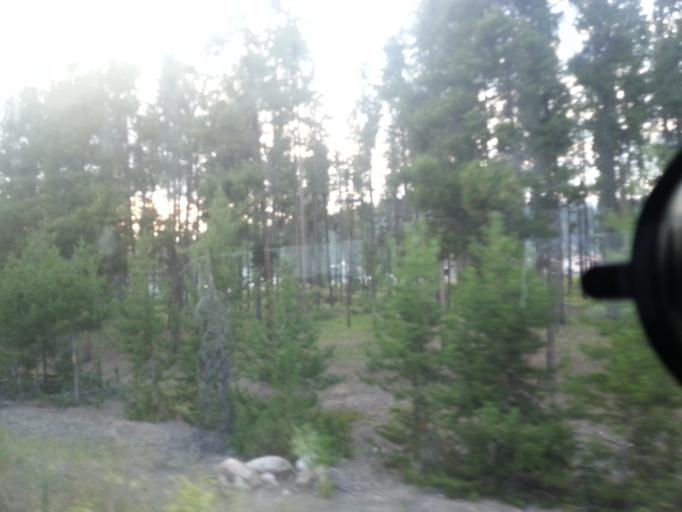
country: CA
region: Alberta
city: Jasper Park Lodge
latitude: 52.8706
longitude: -118.0878
